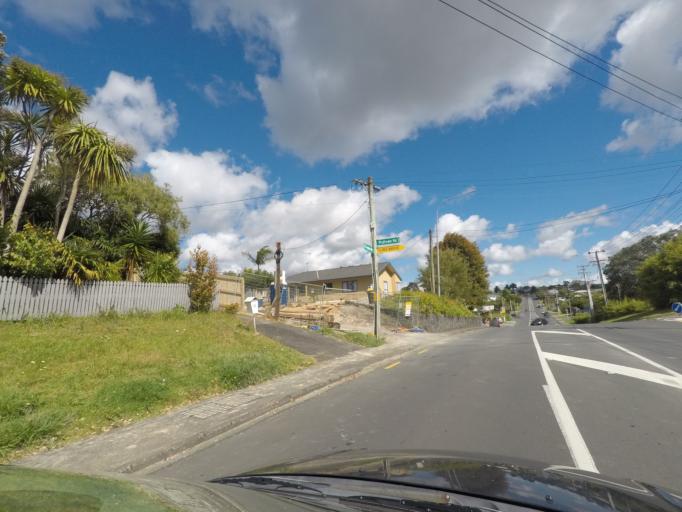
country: NZ
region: Auckland
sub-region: Auckland
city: Waitakere
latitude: -36.9150
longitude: 174.6653
